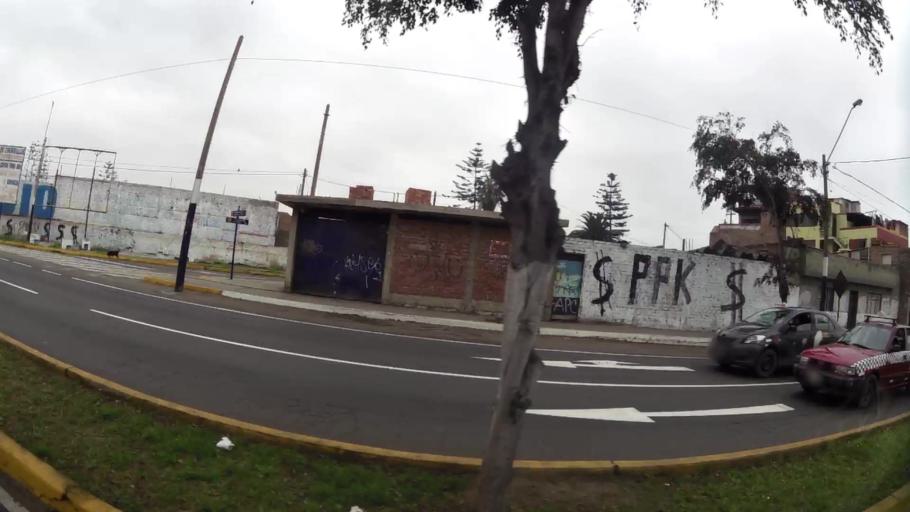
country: PE
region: Lima
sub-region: Lima
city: Surco
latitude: -12.1916
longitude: -77.0073
